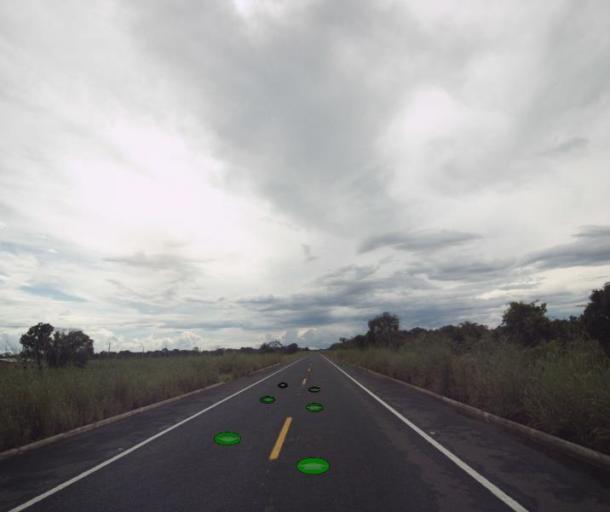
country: BR
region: Goias
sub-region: Sao Miguel Do Araguaia
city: Sao Miguel do Araguaia
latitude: -13.2464
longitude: -50.5340
